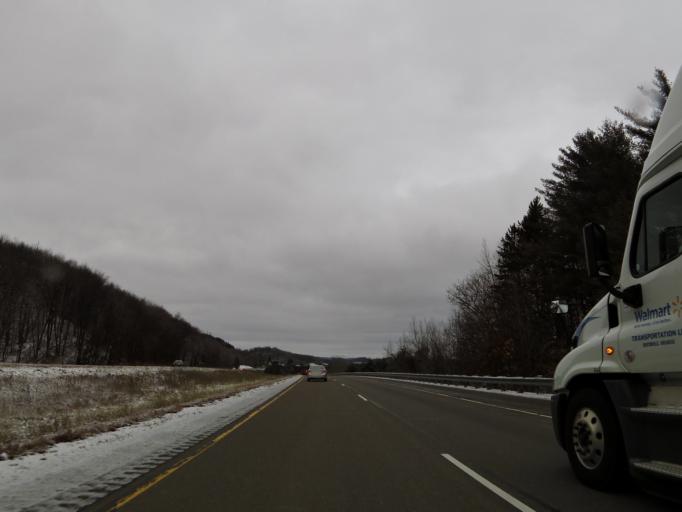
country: US
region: Wisconsin
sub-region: Trempealeau County
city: Osseo
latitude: 44.4376
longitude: -91.0717
